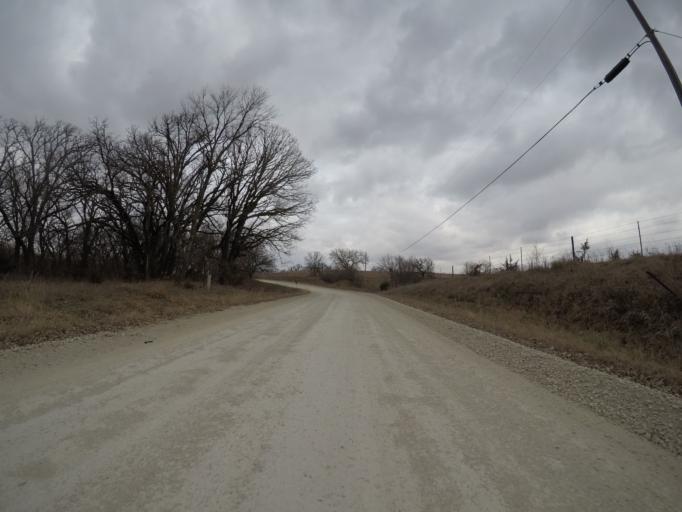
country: US
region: Kansas
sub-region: Morris County
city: Council Grove
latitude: 38.7630
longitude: -96.2794
